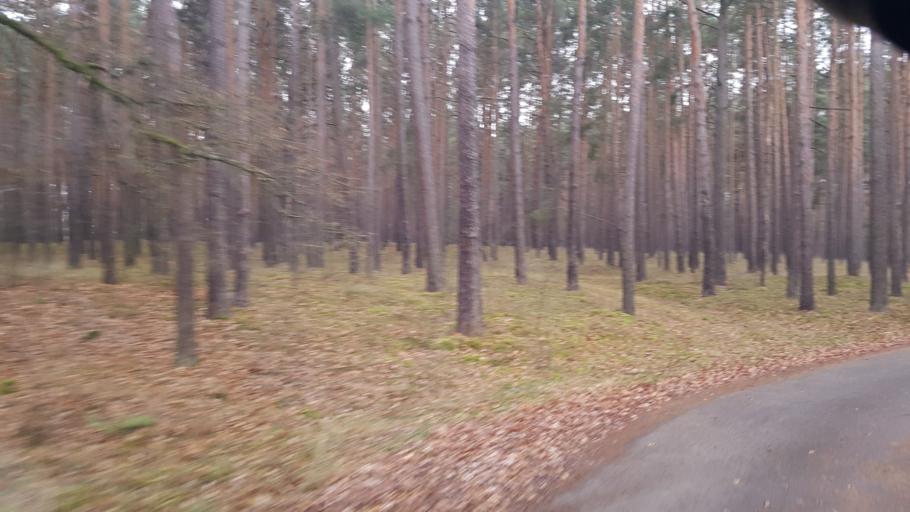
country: DE
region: Brandenburg
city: Schenkendobern
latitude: 51.9808
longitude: 14.6630
